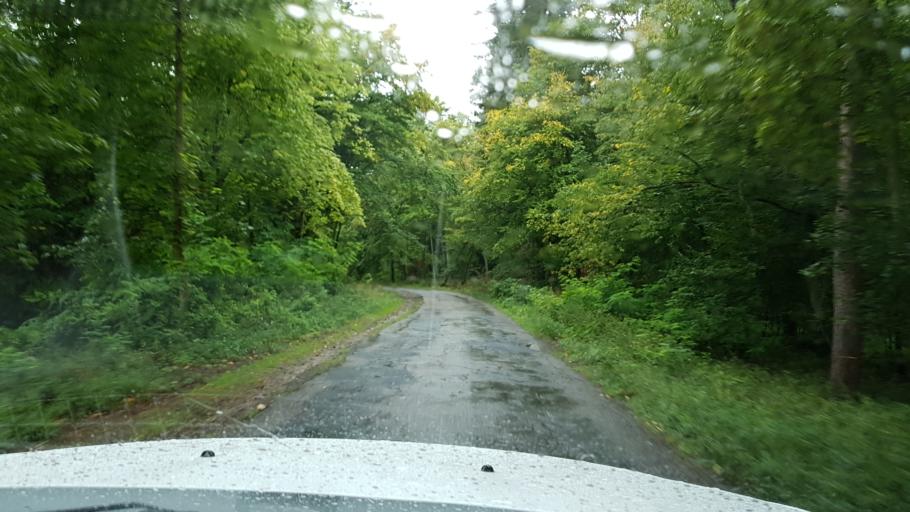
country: DE
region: Brandenburg
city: Meyenburg
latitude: 52.9861
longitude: 14.2645
